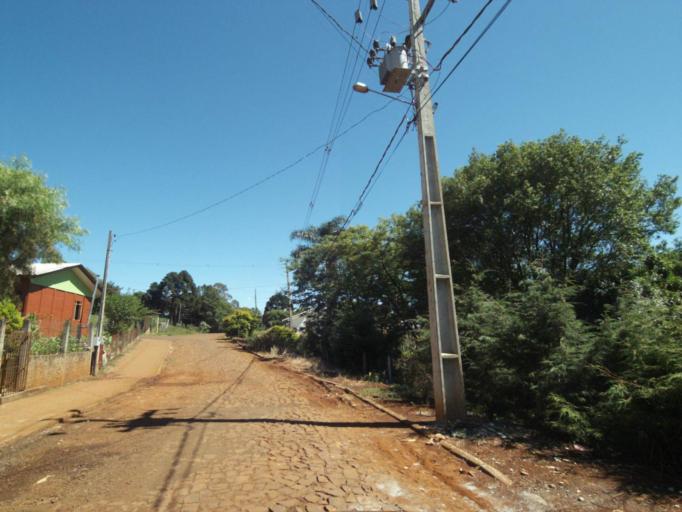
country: BR
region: Santa Catarina
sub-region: Sao Lourenco Do Oeste
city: Sao Lourenco dOeste
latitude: -26.2716
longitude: -52.7782
